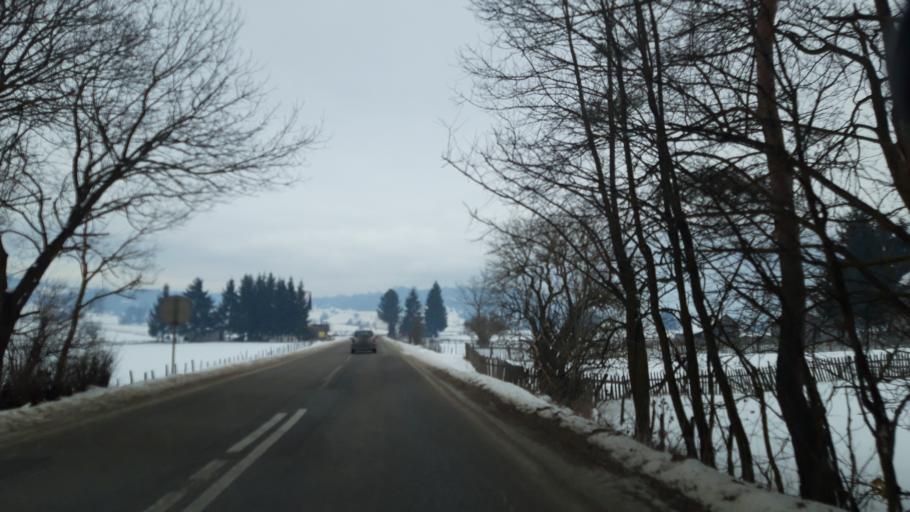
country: BA
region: Republika Srpska
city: Sokolac
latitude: 43.9453
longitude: 18.8330
